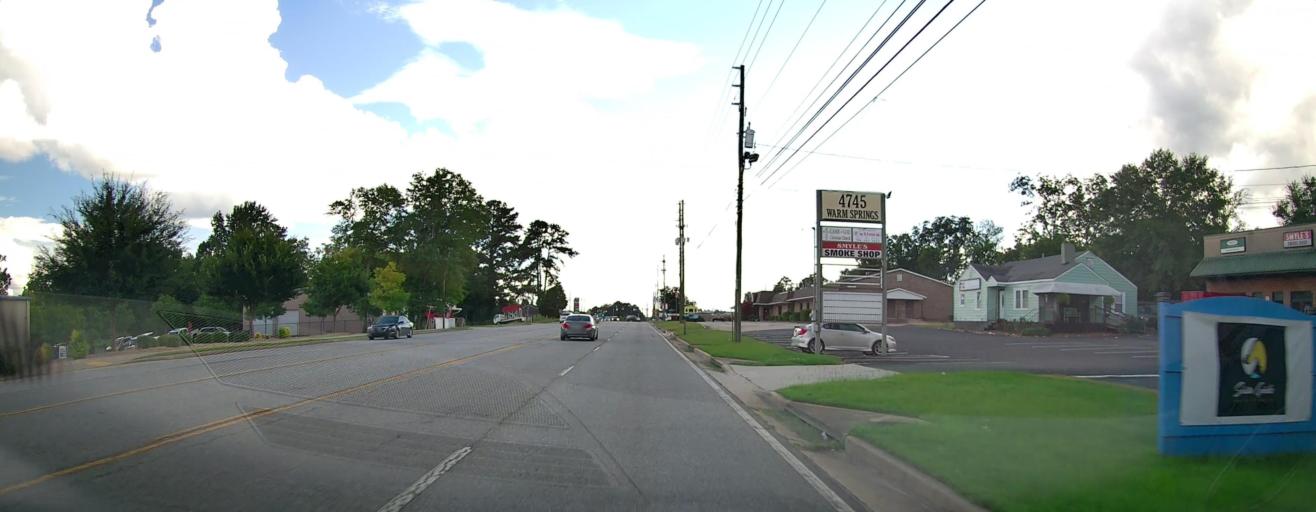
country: US
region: Georgia
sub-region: Muscogee County
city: Columbus
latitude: 32.5265
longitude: -84.9140
